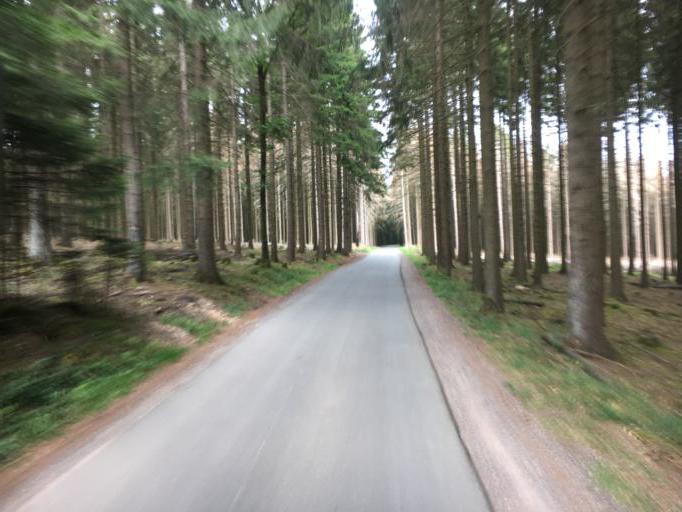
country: DE
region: North Rhine-Westphalia
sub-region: Regierungsbezirk Arnsberg
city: Herscheid
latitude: 51.2081
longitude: 7.7660
